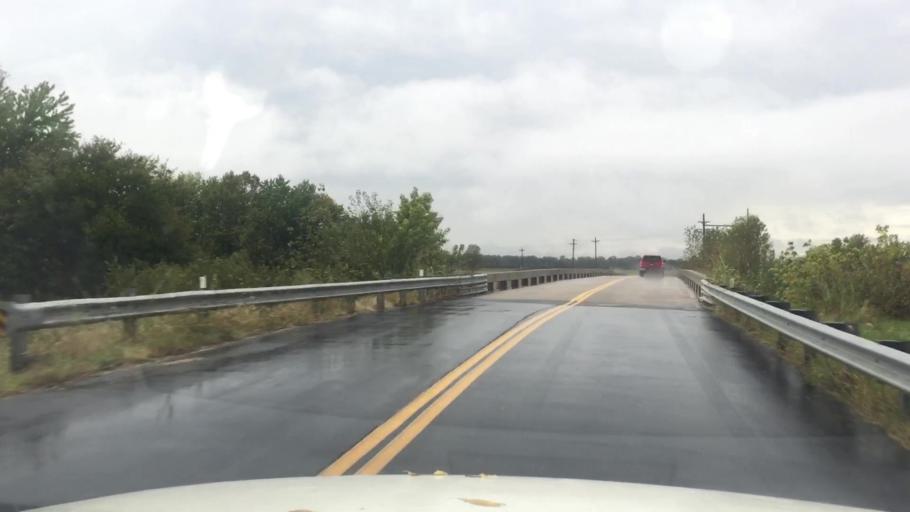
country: US
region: Missouri
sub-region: Boone County
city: Columbia
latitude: 38.8858
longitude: -92.4502
